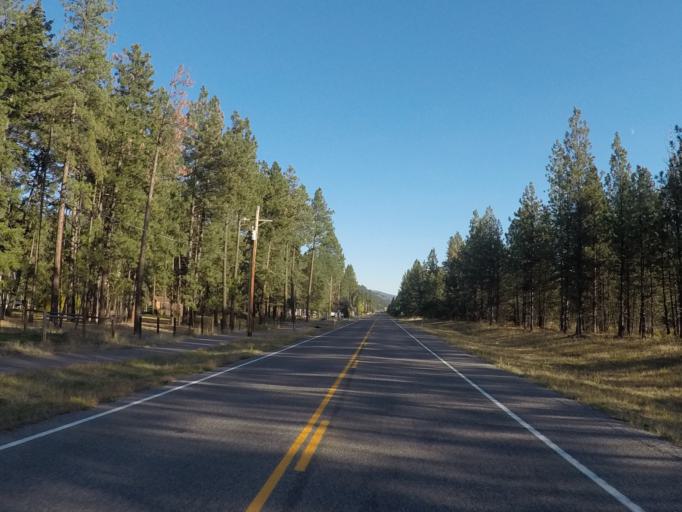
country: US
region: Montana
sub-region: Missoula County
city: Bonner-West Riverside
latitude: 46.8435
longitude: -113.8401
